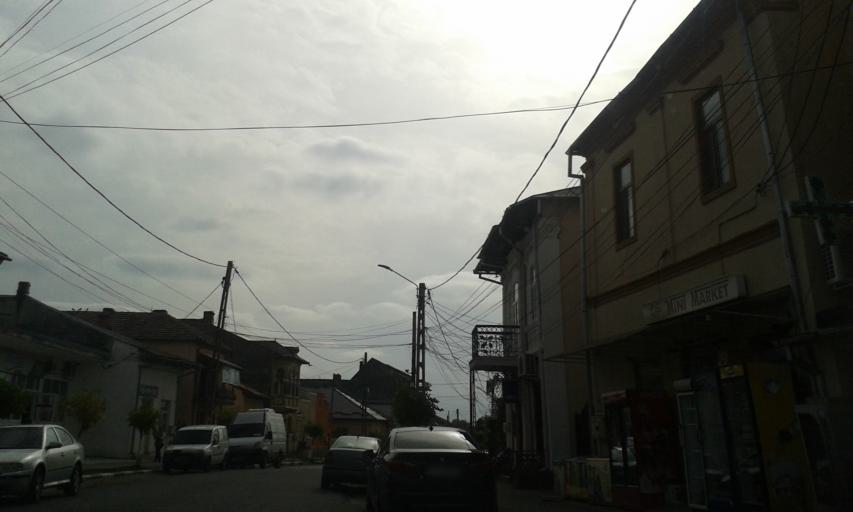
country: RO
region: Gorj
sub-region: Comuna Targu Carbunesti
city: Targu Carbunesti
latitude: 44.9546
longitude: 23.5140
